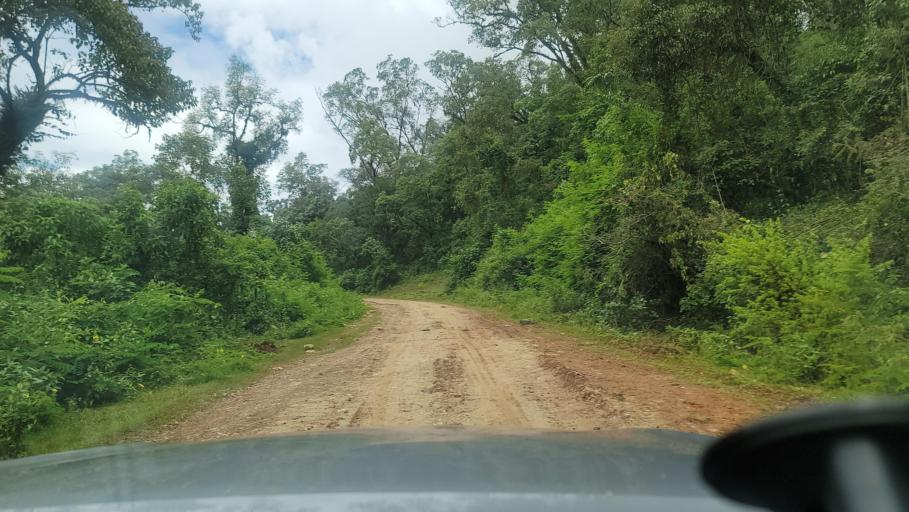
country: ET
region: Southern Nations, Nationalities, and People's Region
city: Bonga
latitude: 7.6290
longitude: 36.2165
